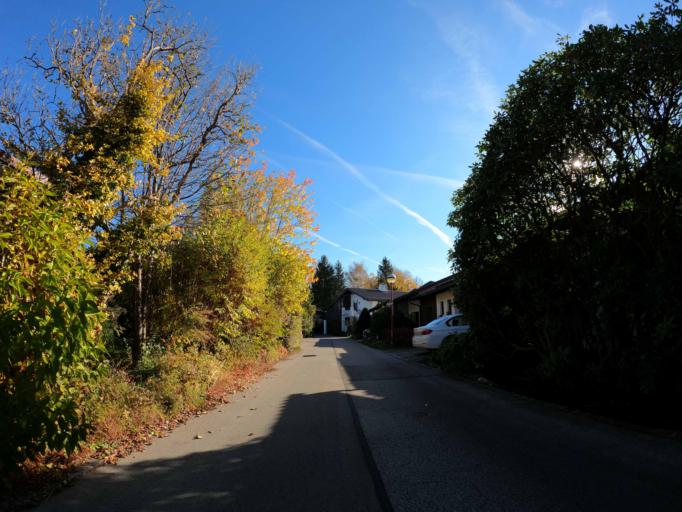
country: DE
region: Bavaria
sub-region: Upper Bavaria
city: Oberhaching
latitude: 48.0240
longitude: 11.6000
